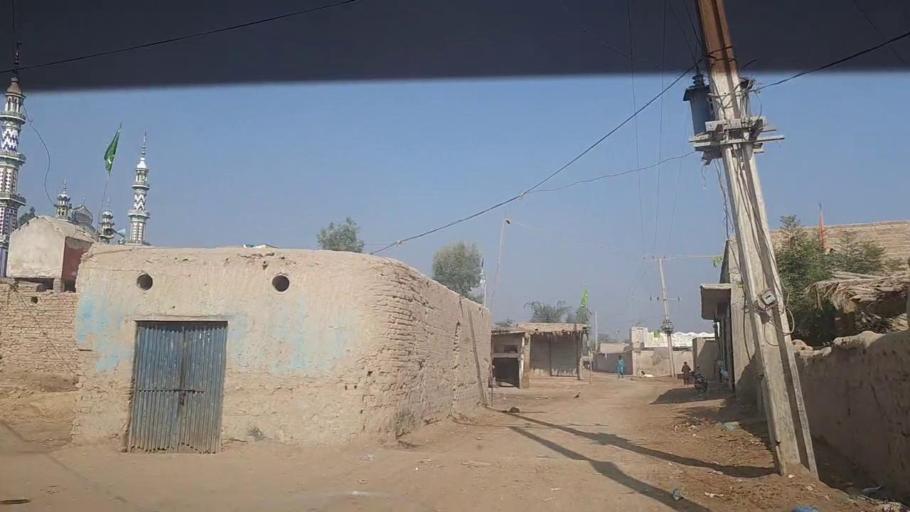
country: PK
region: Sindh
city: Khairpur
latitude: 27.4697
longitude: 68.7132
